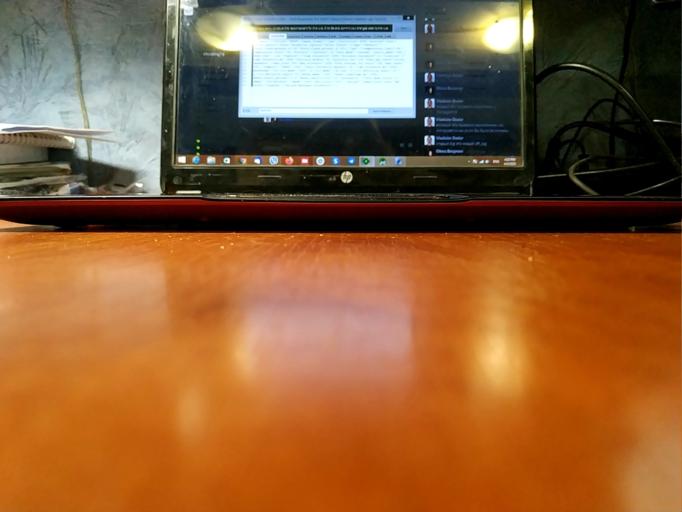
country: RU
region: Tverskaya
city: Sandovo
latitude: 58.5059
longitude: 36.3928
